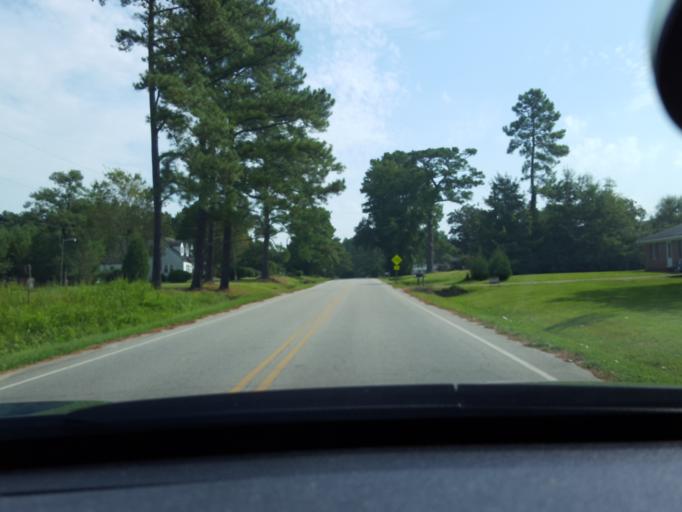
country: US
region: North Carolina
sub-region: Washington County
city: Plymouth
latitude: 35.8693
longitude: -76.7284
